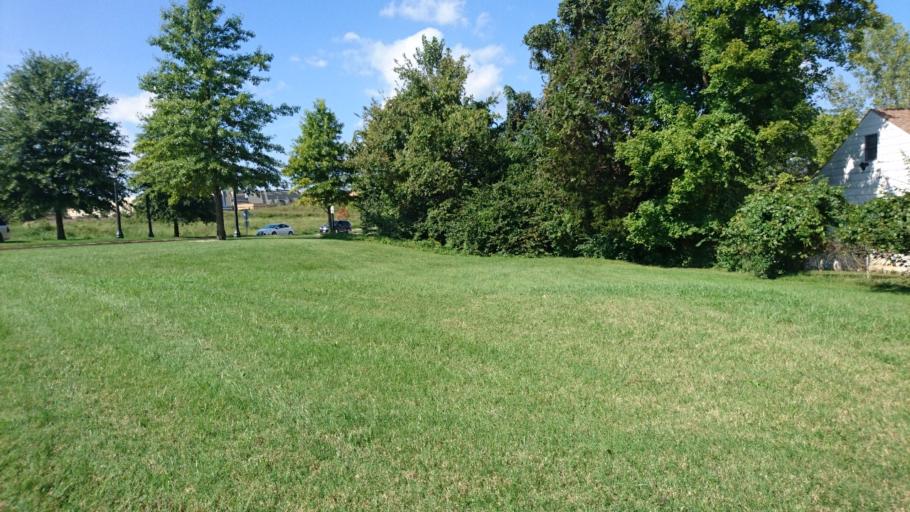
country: US
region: Missouri
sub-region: Saint Louis County
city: Wildwood
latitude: 38.5784
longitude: -90.6272
